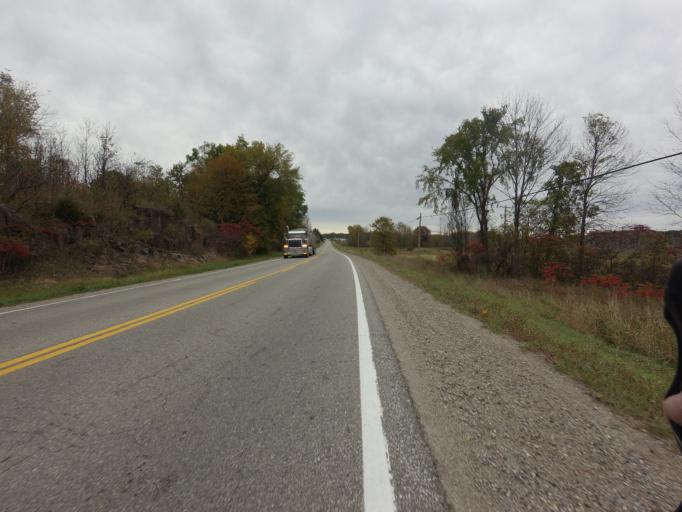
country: CA
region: Ontario
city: Gananoque
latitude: 44.5423
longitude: -76.1350
